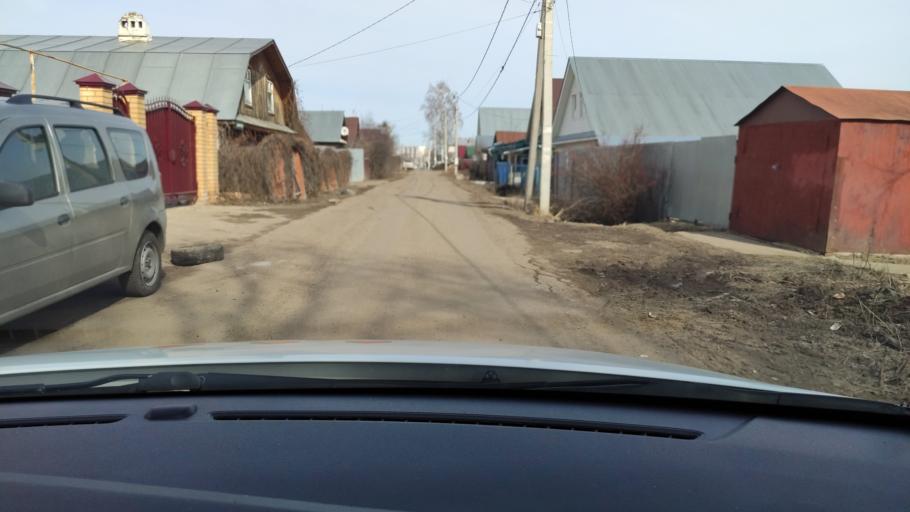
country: RU
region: Tatarstan
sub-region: Gorod Kazan'
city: Kazan
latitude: 55.7280
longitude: 49.1463
